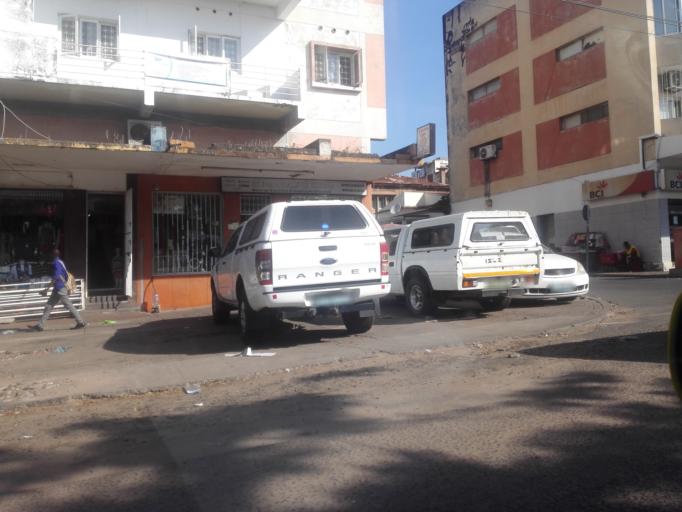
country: MZ
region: Maputo City
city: Maputo
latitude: -25.9617
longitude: 32.5824
